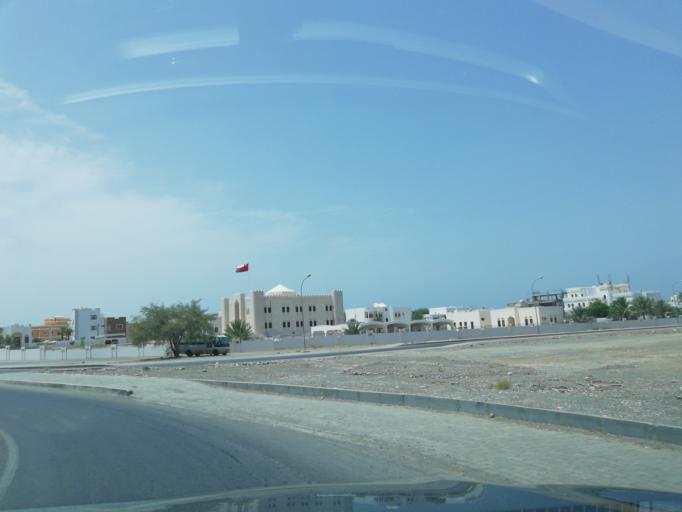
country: OM
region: Muhafazat Masqat
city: As Sib al Jadidah
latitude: 23.6580
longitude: 58.1998
